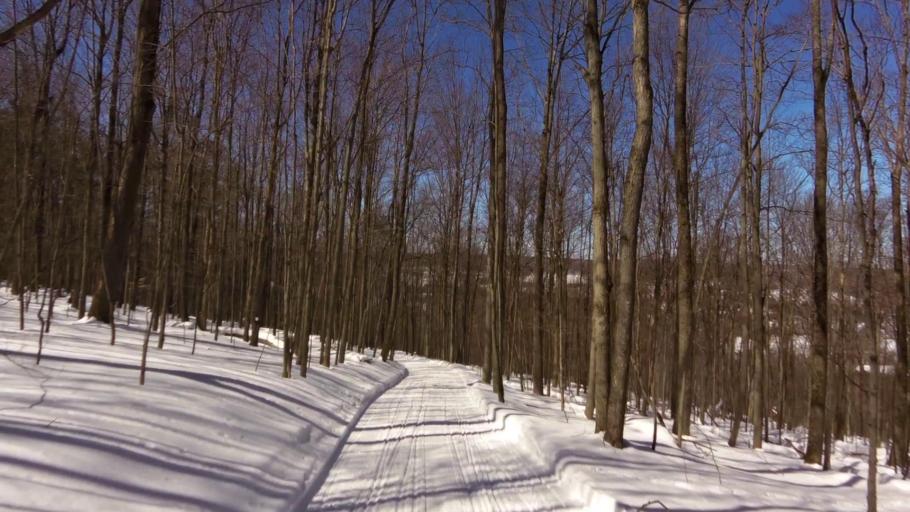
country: US
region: New York
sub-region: Allegany County
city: Houghton
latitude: 42.3760
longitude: -78.2439
